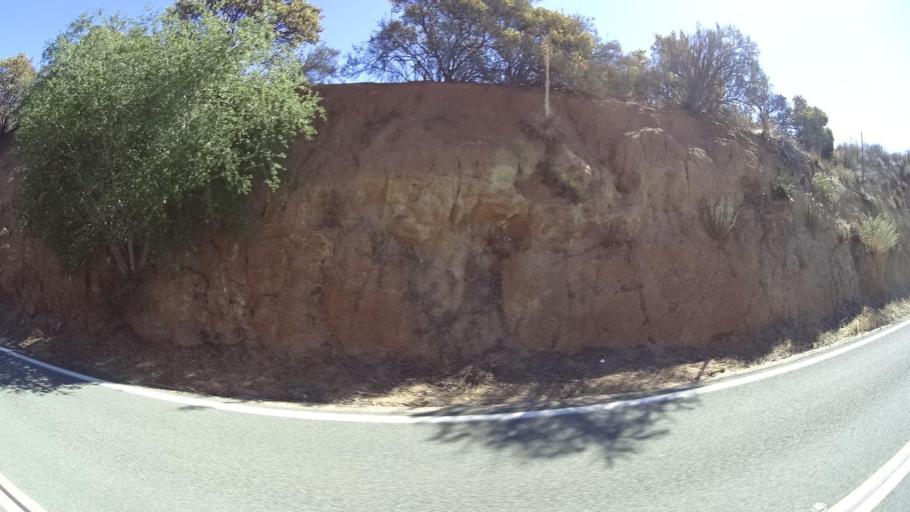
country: US
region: California
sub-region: San Diego County
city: Descanso
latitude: 32.7614
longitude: -116.6741
